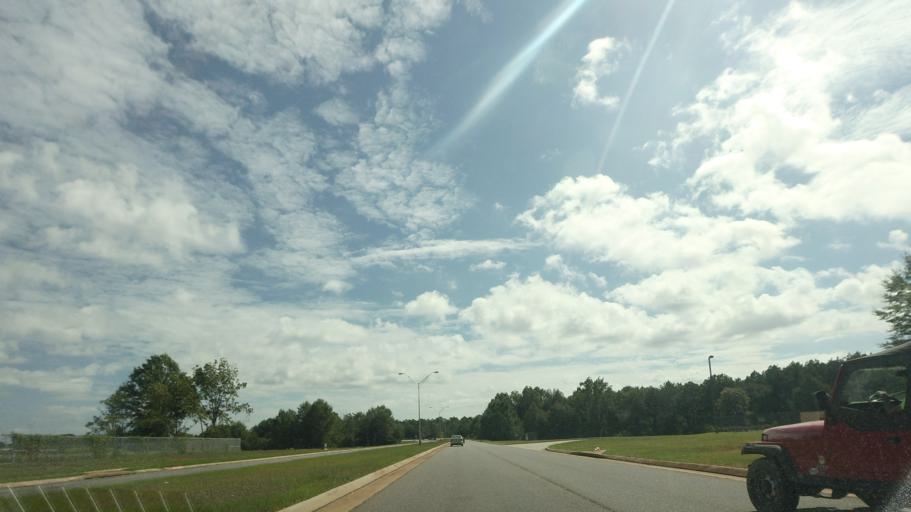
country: US
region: Georgia
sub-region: Houston County
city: Centerville
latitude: 32.5483
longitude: -83.6641
